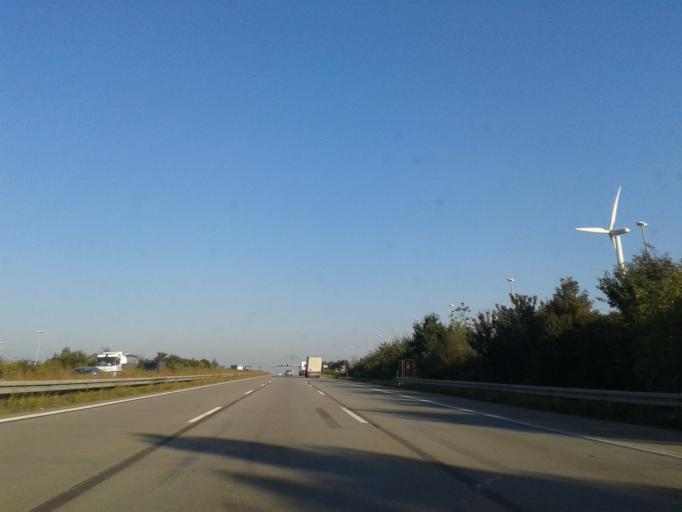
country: DE
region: Saxony
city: Wilsdruff
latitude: 51.0617
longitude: 13.5701
